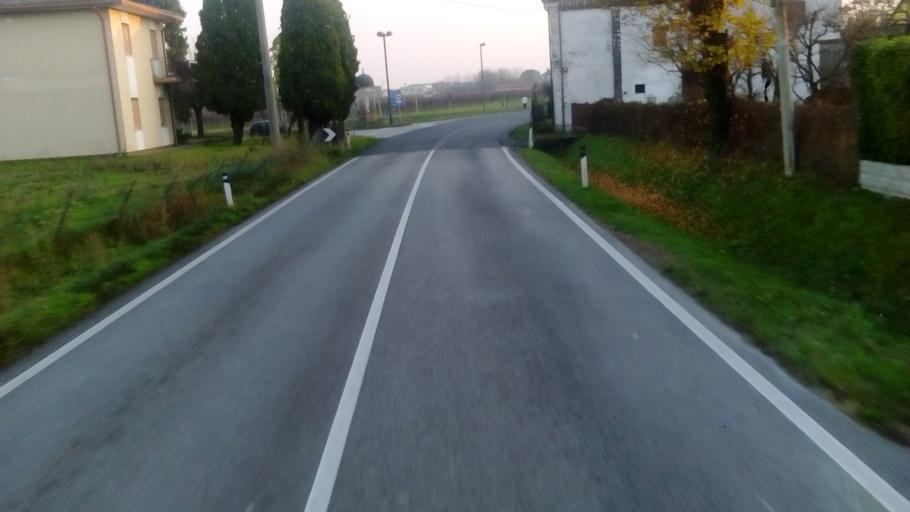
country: IT
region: Veneto
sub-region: Provincia di Padova
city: Tribano
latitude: 45.2184
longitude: 11.8328
